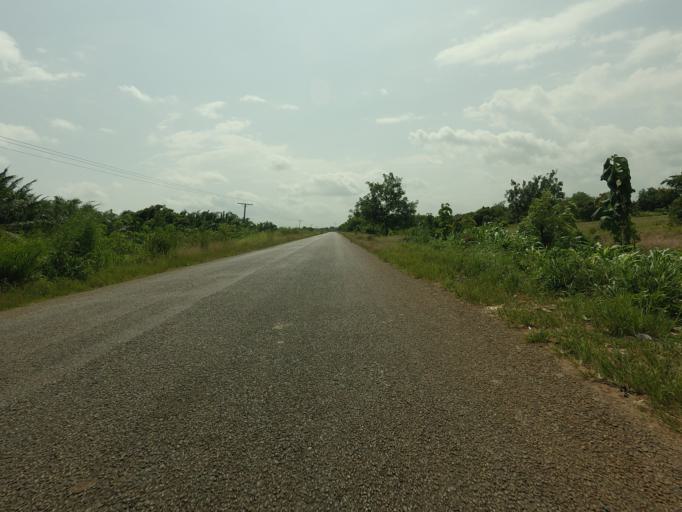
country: TG
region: Maritime
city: Lome
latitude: 6.2445
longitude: 0.9817
